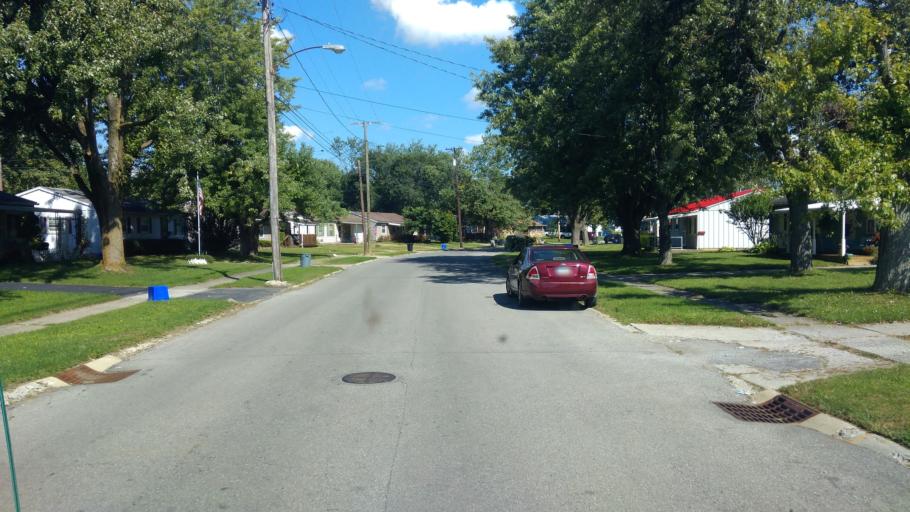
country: US
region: Ohio
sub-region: Marion County
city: Marion
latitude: 40.6075
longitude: -83.1201
